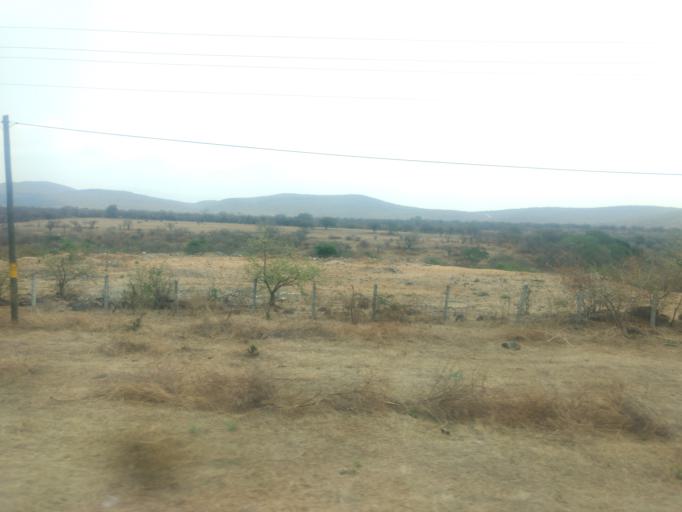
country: MX
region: Morelos
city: La Joya
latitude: 18.6709
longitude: -99.4311
